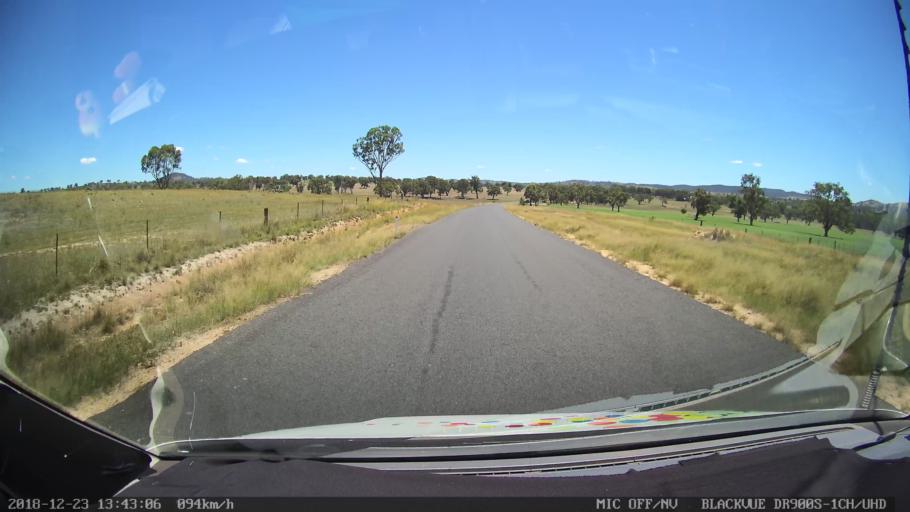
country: AU
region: New South Wales
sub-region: Tamworth Municipality
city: Manilla
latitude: -30.4834
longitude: 151.1551
